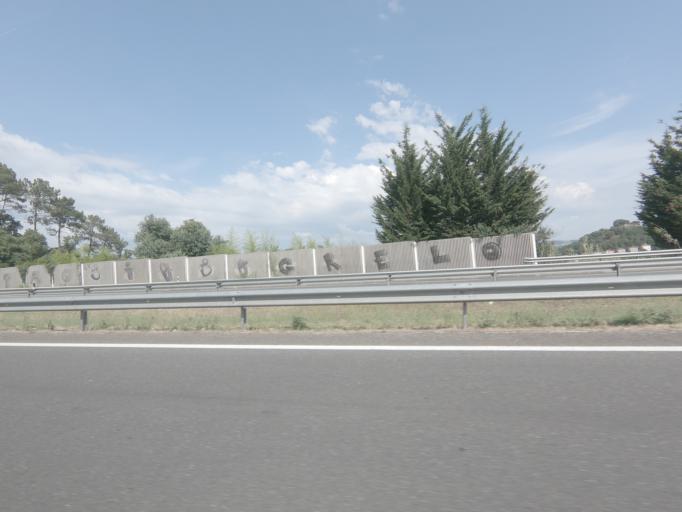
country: ES
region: Galicia
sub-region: Provincia de Ourense
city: Ourense
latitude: 42.3351
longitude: -7.8862
